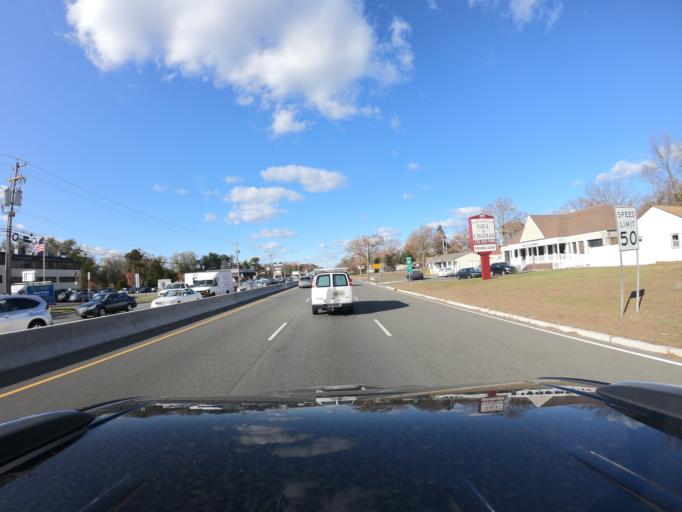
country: US
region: New Jersey
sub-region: Ocean County
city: Lakewood
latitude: 40.1573
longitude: -74.2308
